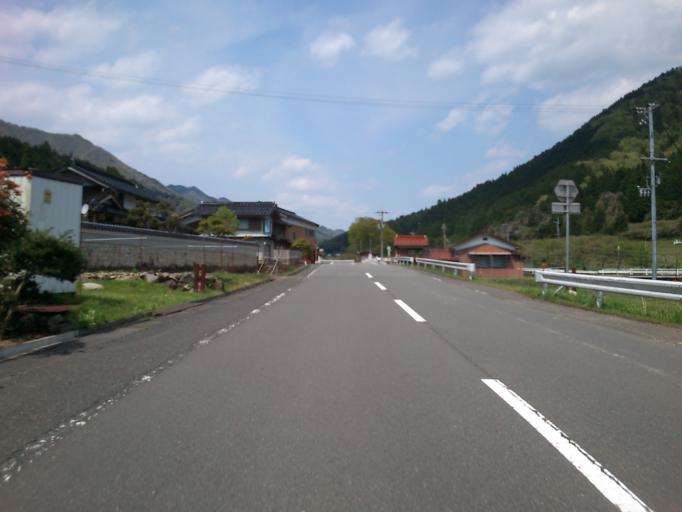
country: JP
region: Kyoto
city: Fukuchiyama
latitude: 35.3667
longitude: 134.9388
